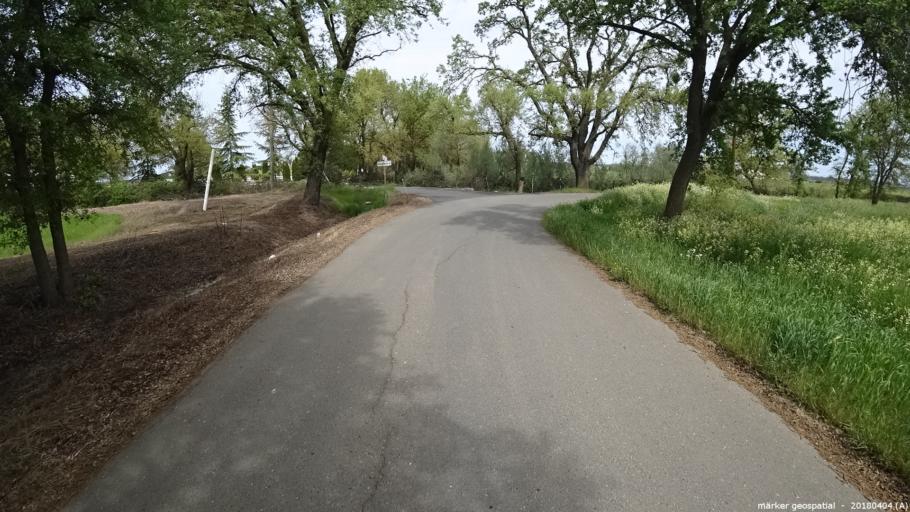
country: US
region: California
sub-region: Sacramento County
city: Herald
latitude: 38.2778
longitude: -121.1897
